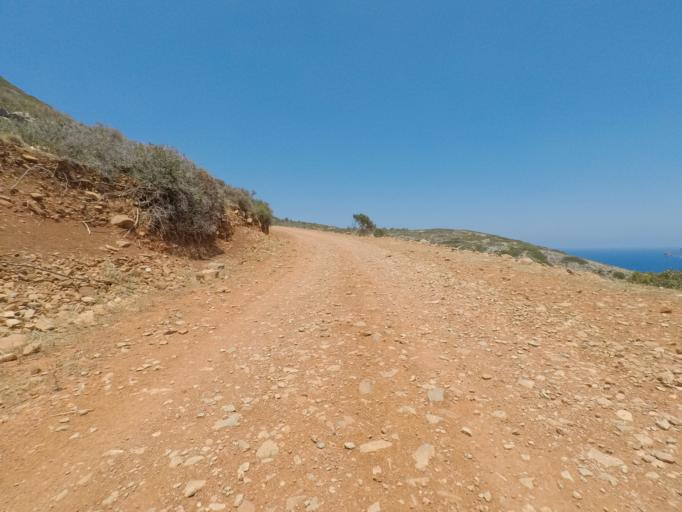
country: GR
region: Crete
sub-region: Nomos Lasithiou
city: Elounda
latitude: 35.3198
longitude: 25.7568
